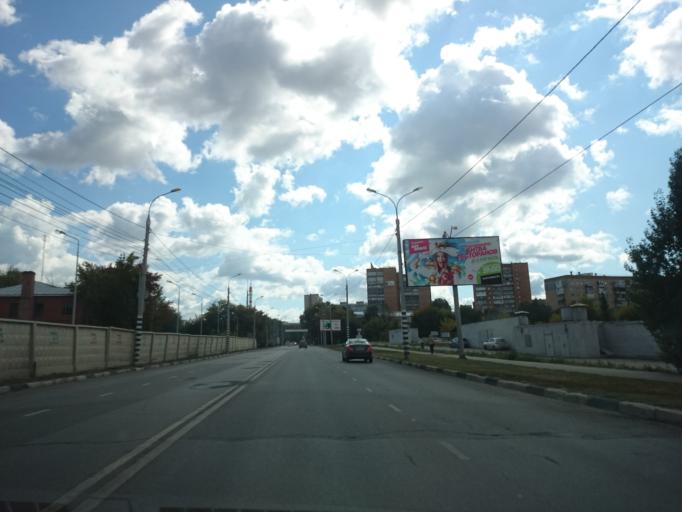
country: RU
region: Samara
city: Samara
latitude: 53.2151
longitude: 50.1384
